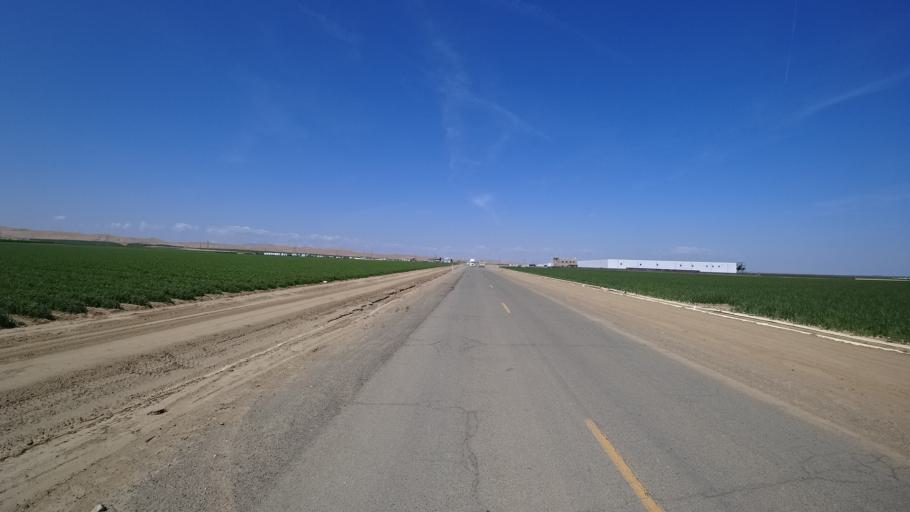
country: US
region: California
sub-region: Kings County
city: Kettleman City
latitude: 36.0725
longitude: -120.0427
